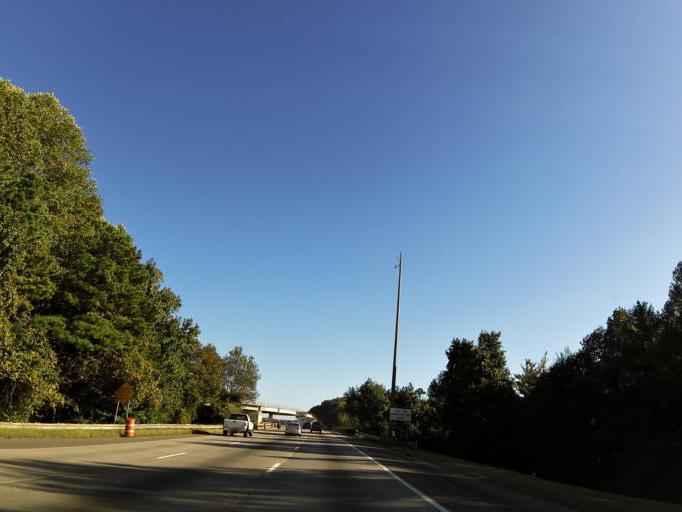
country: US
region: Georgia
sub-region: Cobb County
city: Kennesaw
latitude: 34.0107
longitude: -84.5686
